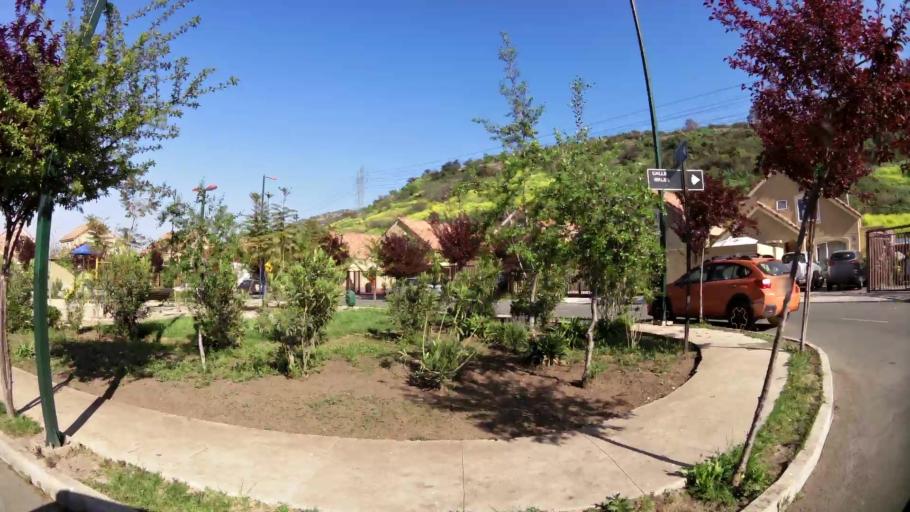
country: CL
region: Santiago Metropolitan
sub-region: Provincia de Chacabuco
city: Chicureo Abajo
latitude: -33.3457
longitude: -70.6784
